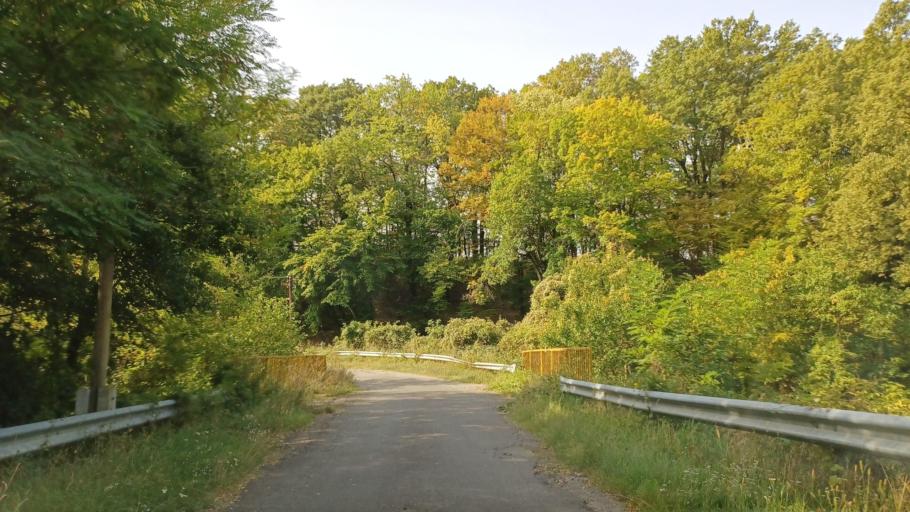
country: HU
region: Baranya
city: Mecseknadasd
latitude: 46.1923
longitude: 18.4491
